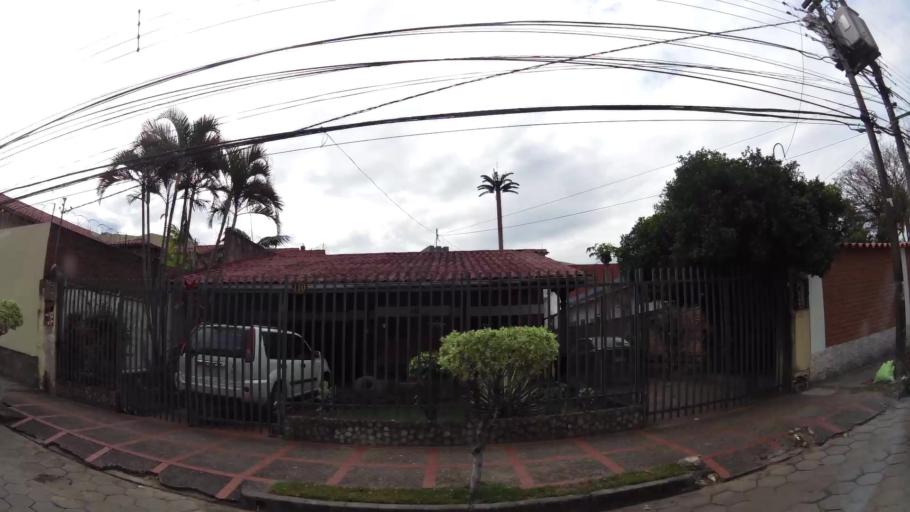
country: BO
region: Santa Cruz
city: Santa Cruz de la Sierra
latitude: -17.7965
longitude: -63.1960
